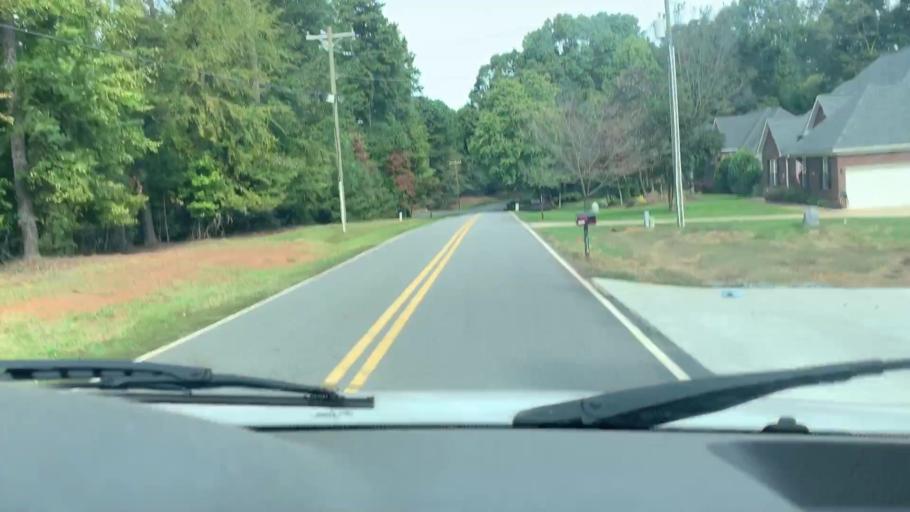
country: US
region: North Carolina
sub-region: Catawba County
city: Lake Norman of Catawba
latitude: 35.5734
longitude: -80.9422
